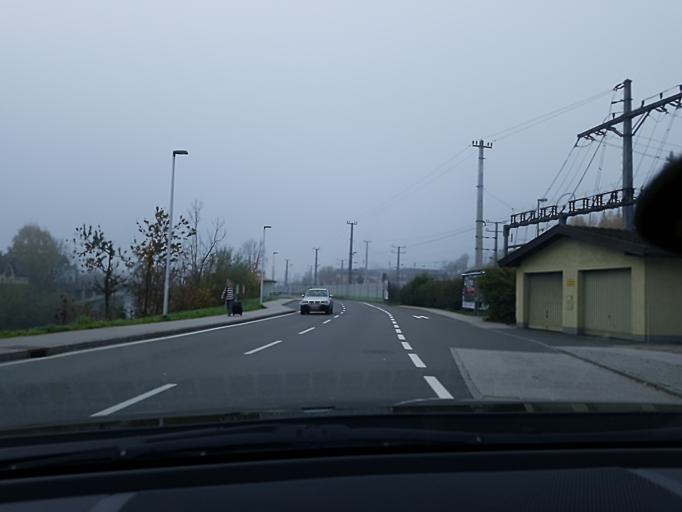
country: AT
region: Salzburg
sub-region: Politischer Bezirk Sankt Johann im Pongau
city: Sankt Johann im Pongau
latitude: 47.3481
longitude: 13.1954
